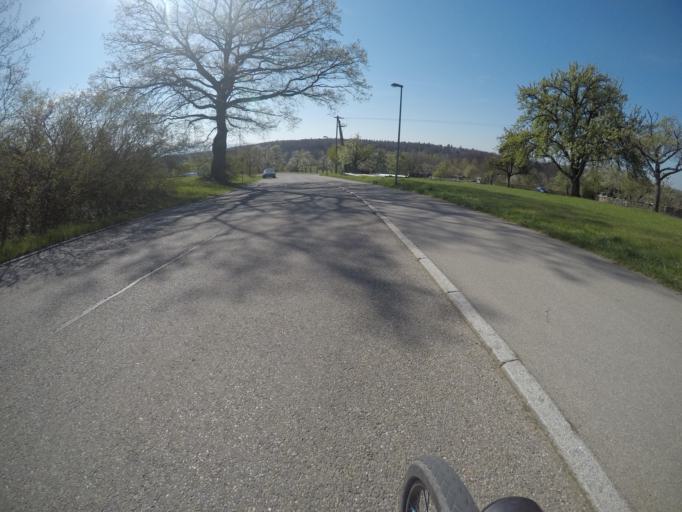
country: DE
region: Baden-Wuerttemberg
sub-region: Regierungsbezirk Stuttgart
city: Filderstadt
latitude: 48.6479
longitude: 9.1927
